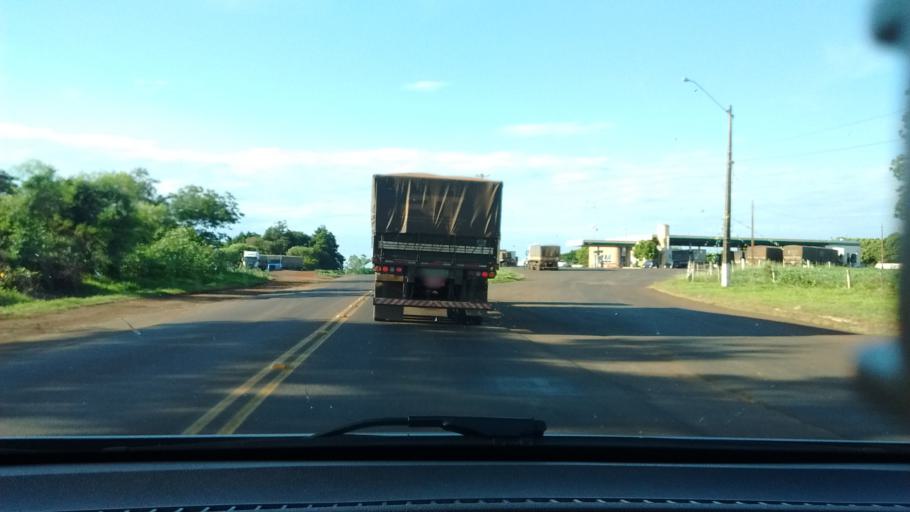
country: BR
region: Parana
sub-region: Cascavel
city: Cascavel
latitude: -25.1897
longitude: -53.6012
